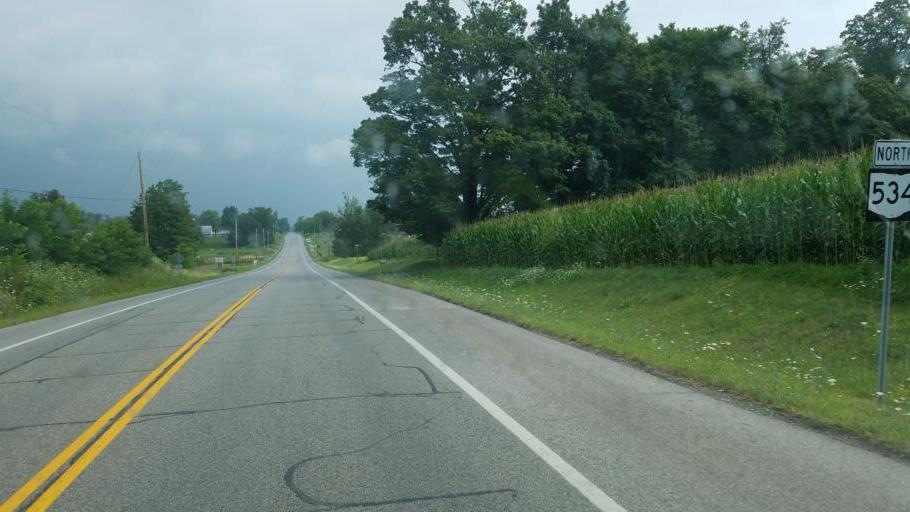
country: US
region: Ohio
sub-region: Ashtabula County
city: Orwell
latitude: 41.4675
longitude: -80.9531
